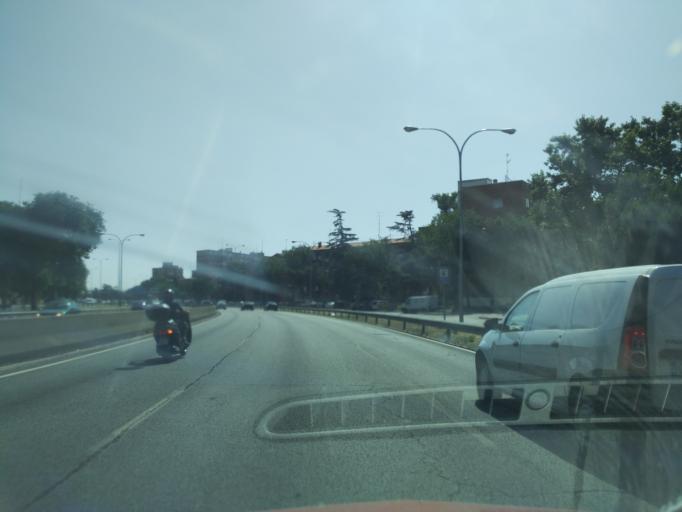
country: ES
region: Madrid
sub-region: Provincia de Madrid
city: Usera
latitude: 40.3900
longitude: -3.7121
